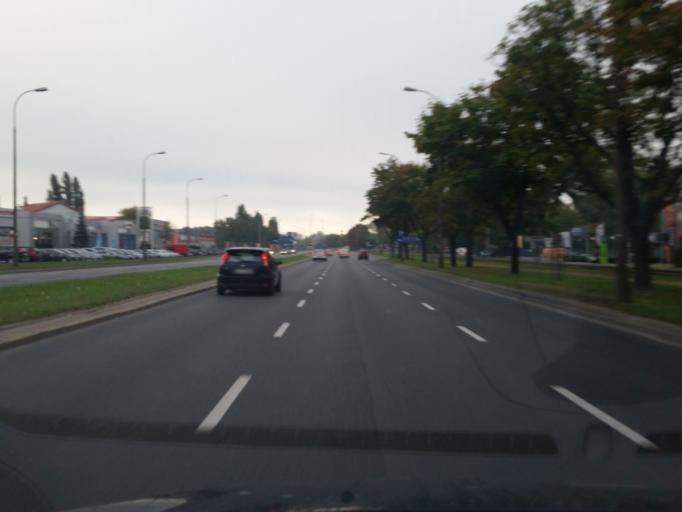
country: PL
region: Masovian Voivodeship
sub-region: Warszawa
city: Zoliborz
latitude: 52.2761
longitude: 21.0133
